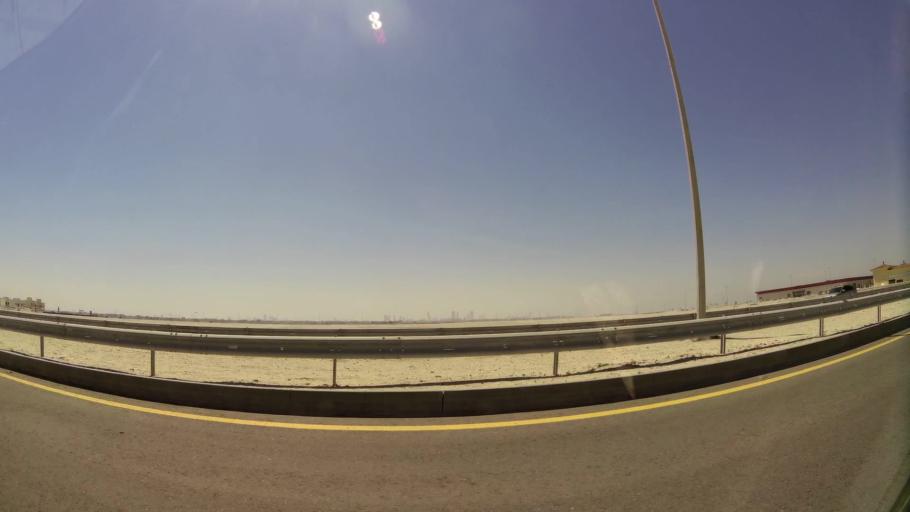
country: BH
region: Muharraq
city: Al Muharraq
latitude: 26.3051
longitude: 50.6304
